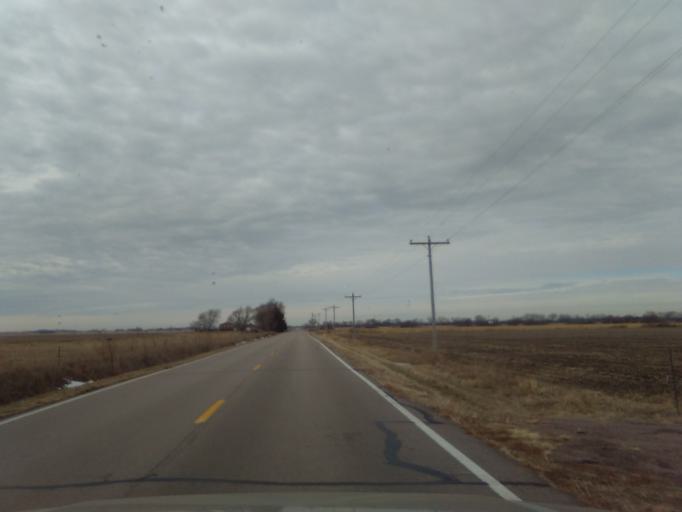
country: US
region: Nebraska
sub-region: Hall County
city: Grand Island
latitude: 40.7709
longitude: -98.4187
